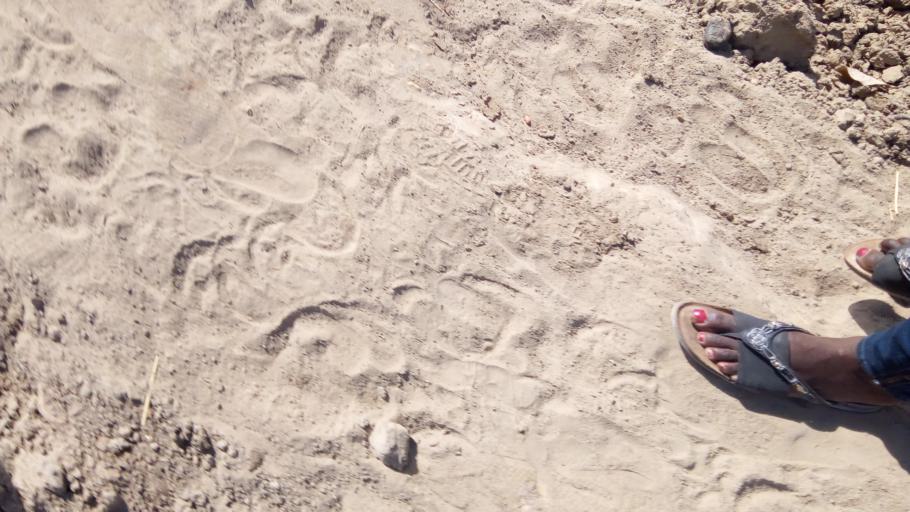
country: ML
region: Kayes
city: Diema
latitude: 14.5132
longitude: -8.8392
